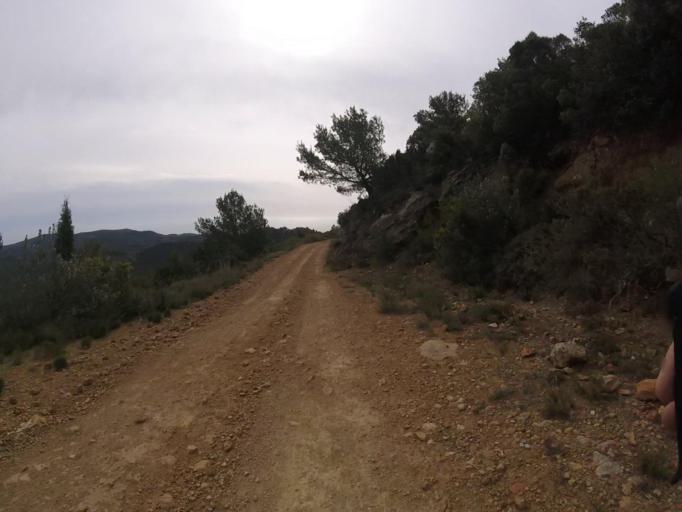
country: ES
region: Valencia
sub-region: Provincia de Castello
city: Benicassim
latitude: 40.0869
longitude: 0.0395
